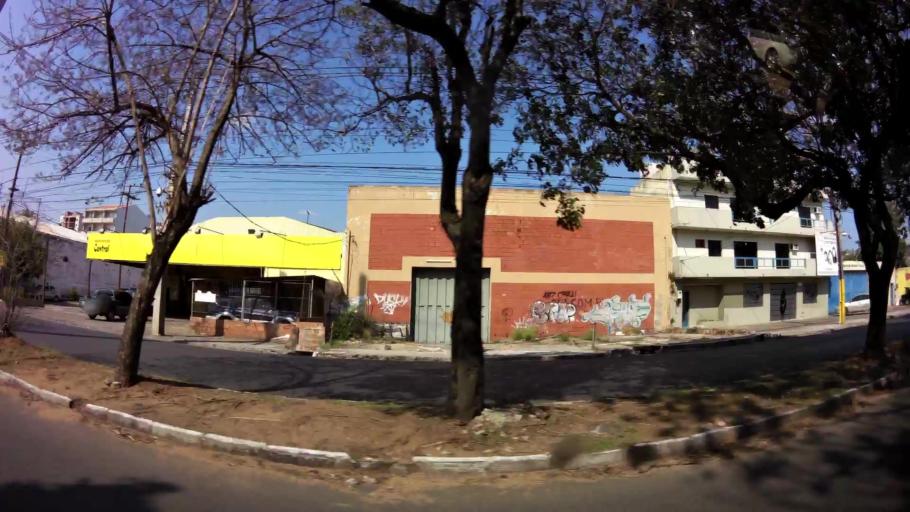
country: PY
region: Asuncion
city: Asuncion
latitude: -25.3207
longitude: -57.6289
